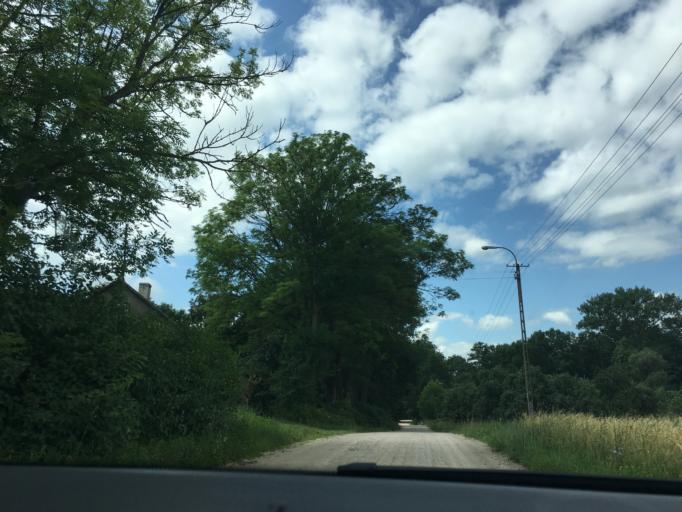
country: PL
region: Podlasie
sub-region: Powiat sejnenski
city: Krasnopol
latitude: 54.0881
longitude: 23.2484
